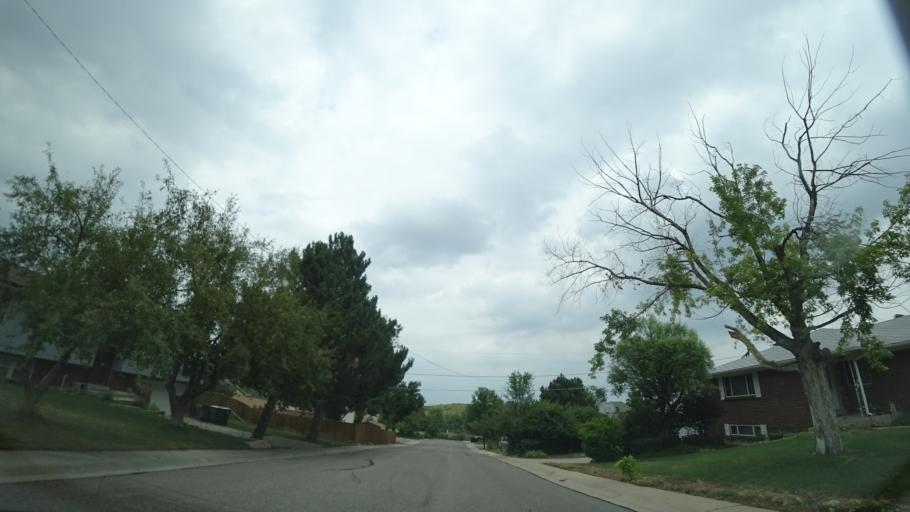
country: US
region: Colorado
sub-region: Jefferson County
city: West Pleasant View
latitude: 39.7086
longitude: -105.1526
